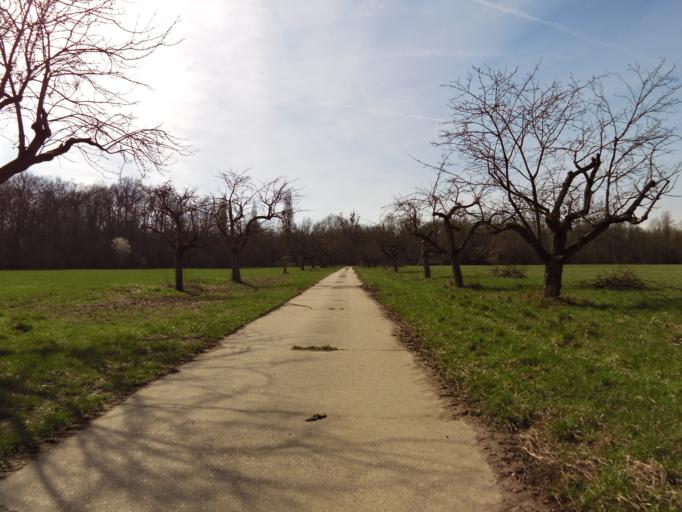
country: DE
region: Hesse
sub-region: Regierungsbezirk Darmstadt
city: Stockstadt am Rhein
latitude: 49.8128
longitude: 8.4273
